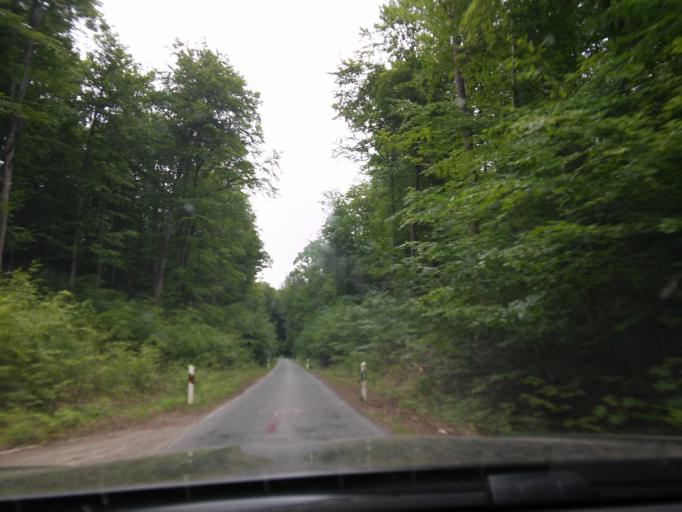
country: DE
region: Thuringia
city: Sondershausen
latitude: 51.3440
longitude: 10.8515
